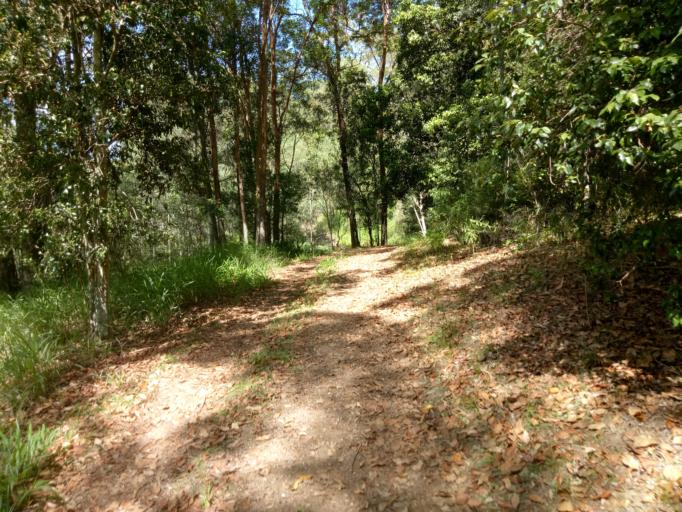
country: AU
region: Queensland
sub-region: Moreton Bay
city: Ferny Hills
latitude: -27.4469
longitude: 152.9119
